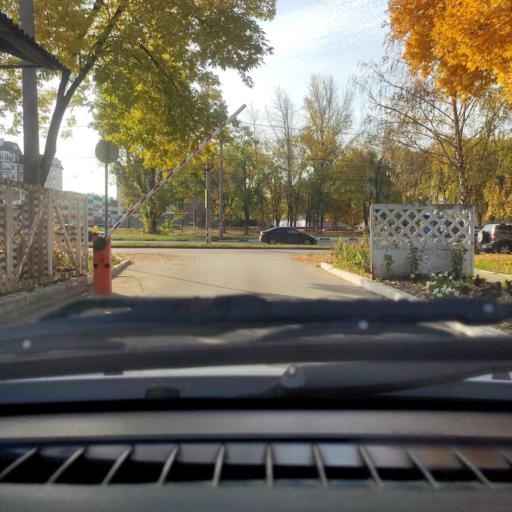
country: RU
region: Samara
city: Tol'yatti
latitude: 53.5002
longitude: 49.4120
